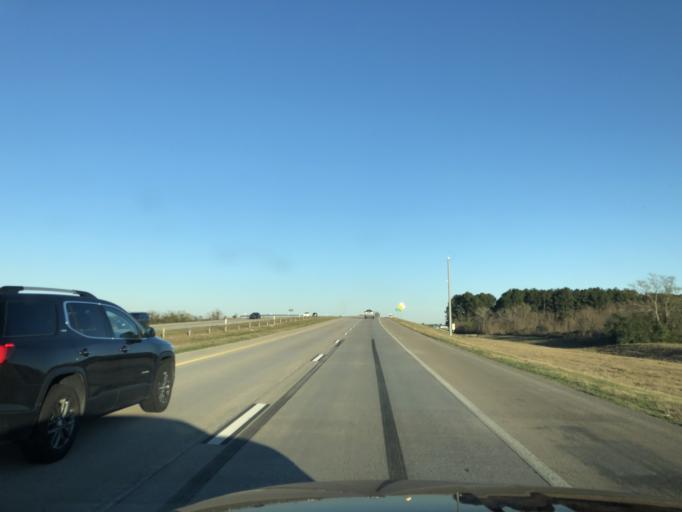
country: US
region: Texas
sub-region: Harris County
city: Cypress
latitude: 30.0540
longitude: -95.7200
